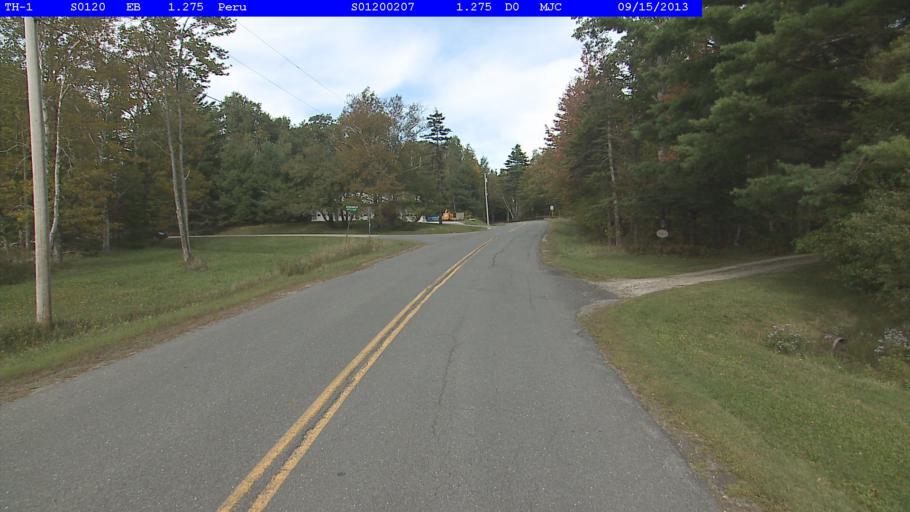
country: US
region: Vermont
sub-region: Bennington County
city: Manchester Center
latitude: 43.2435
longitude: -72.8940
